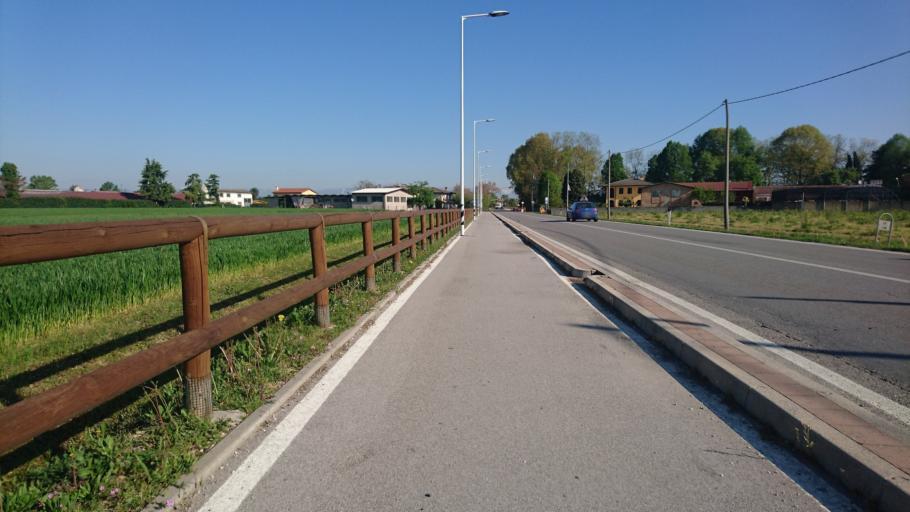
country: IT
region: Veneto
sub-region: Provincia di Padova
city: Massanzago-Ca' Baglioni-San Dono
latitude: 45.5632
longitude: 12.0042
